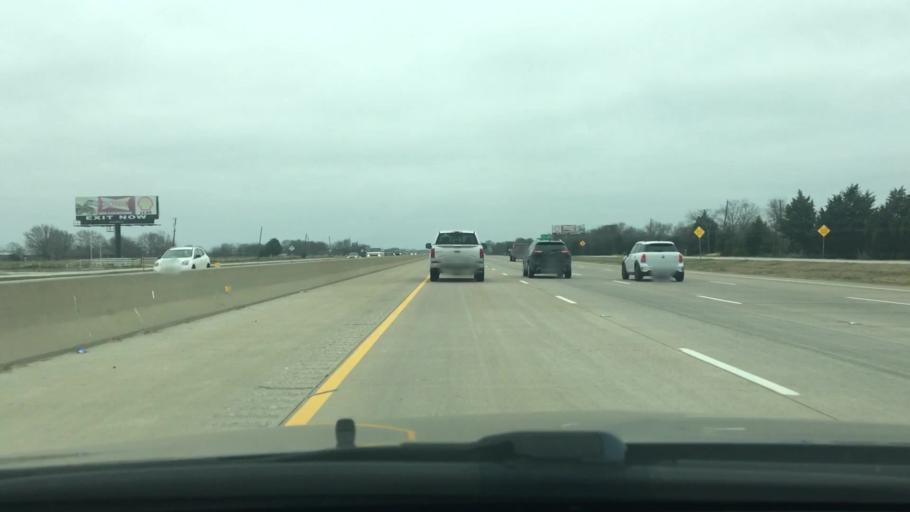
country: US
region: Texas
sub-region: Ellis County
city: Ennis
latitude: 32.2541
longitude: -96.5020
